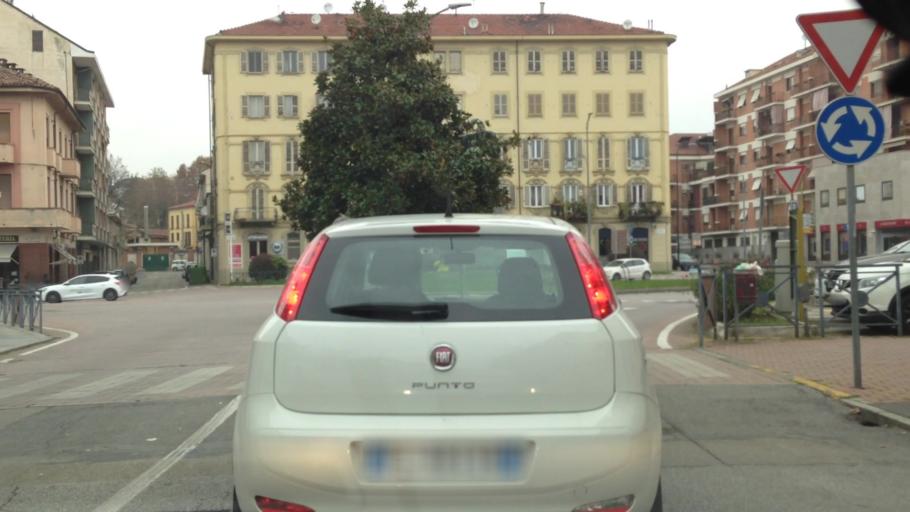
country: IT
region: Piedmont
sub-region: Provincia di Asti
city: Asti
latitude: 44.9026
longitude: 8.2140
